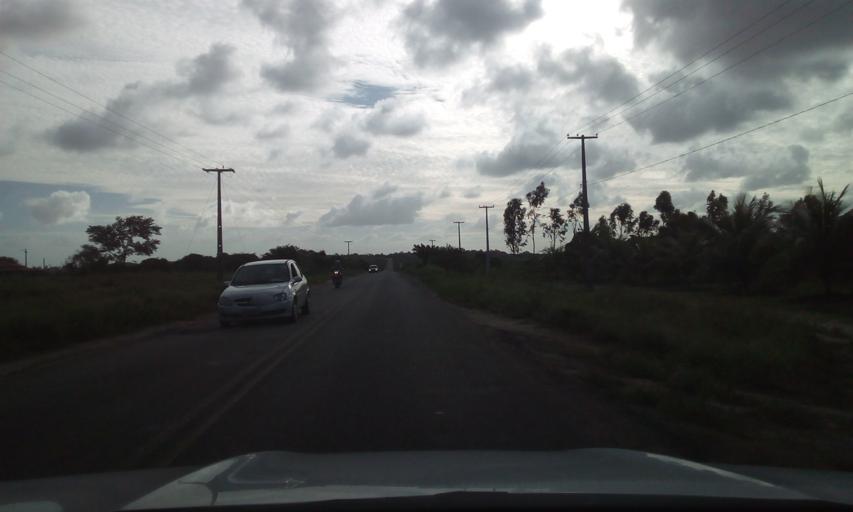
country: BR
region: Paraiba
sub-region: Conde
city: Conde
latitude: -7.2678
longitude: -34.8241
